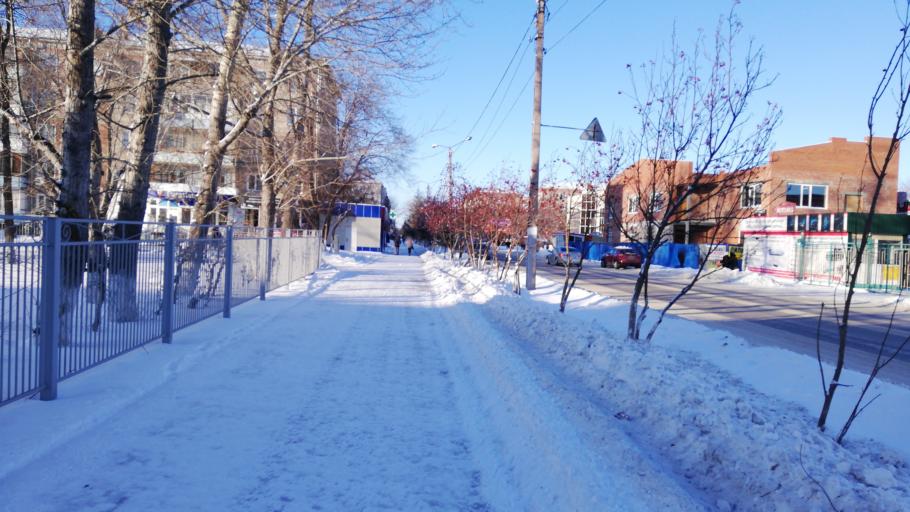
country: KZ
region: Soltustik Qazaqstan
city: Petropavlovsk
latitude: 54.8636
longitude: 69.1454
